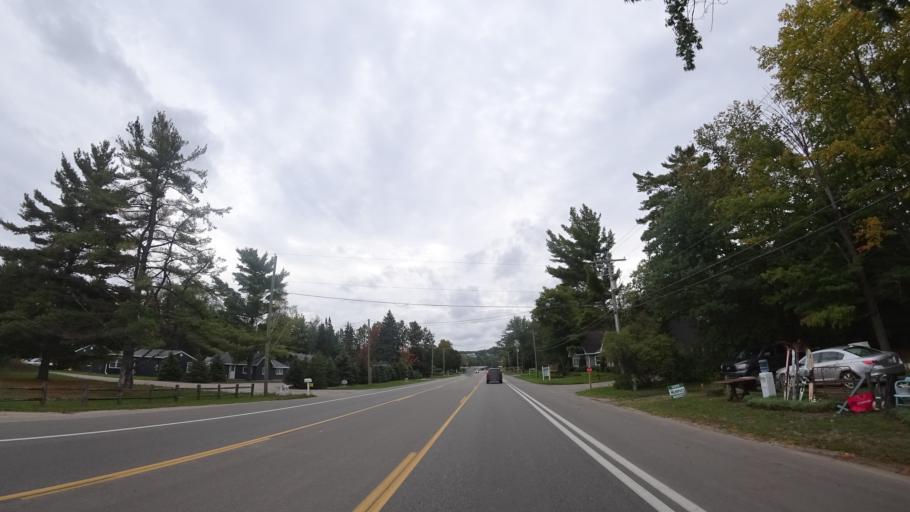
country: US
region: Michigan
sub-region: Emmet County
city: Petoskey
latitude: 45.4024
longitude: -84.9021
